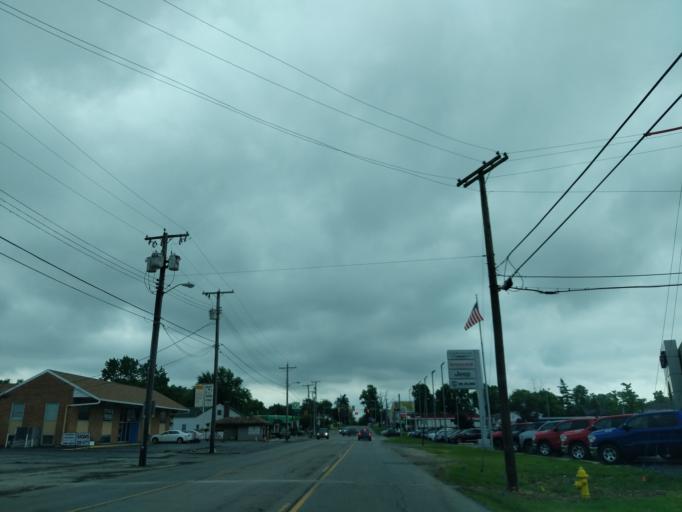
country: US
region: Indiana
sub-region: Delaware County
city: Muncie
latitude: 40.2102
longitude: -85.3976
